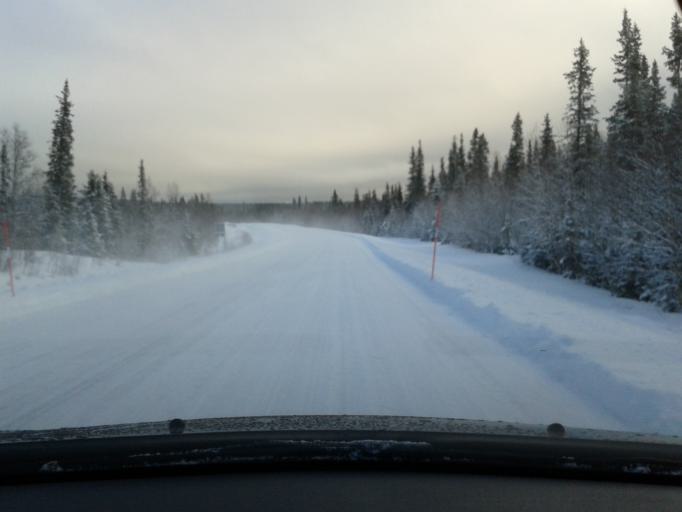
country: SE
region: Vaesterbotten
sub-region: Vilhelmina Kommun
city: Sjoberg
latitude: 65.2571
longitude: 15.7028
